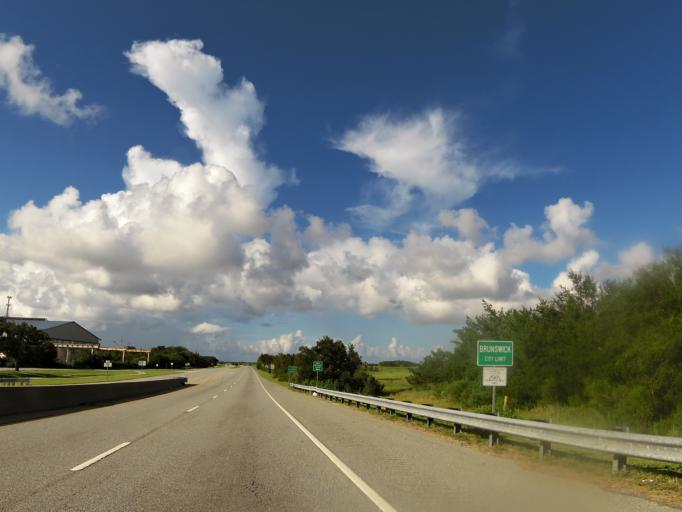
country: US
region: Georgia
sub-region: Glynn County
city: Brunswick
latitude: 31.1268
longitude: -81.4802
